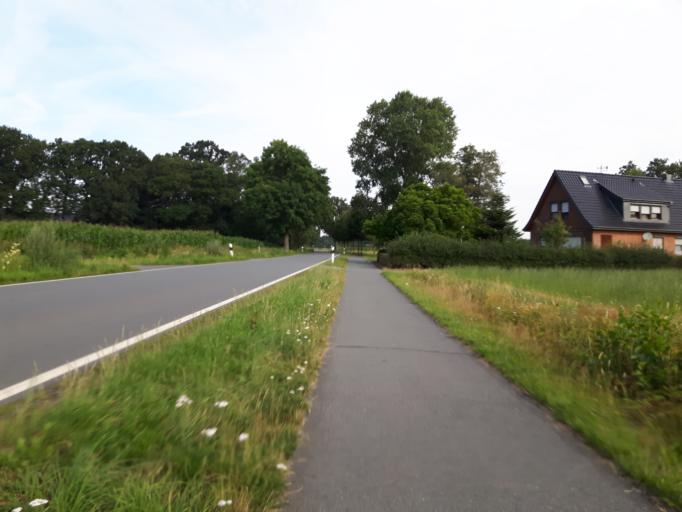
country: DE
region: Lower Saxony
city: Delmenhorst
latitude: 53.0973
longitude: 8.5948
